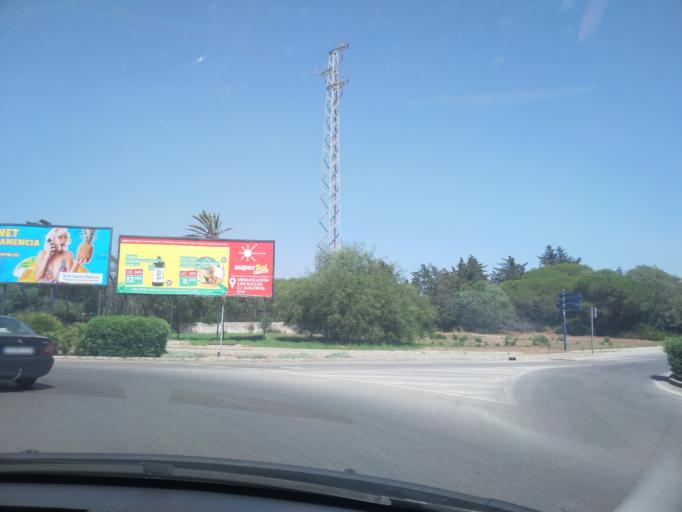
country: ES
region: Andalusia
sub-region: Provincia de Cadiz
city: Chiclana de la Frontera
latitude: 36.3835
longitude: -6.1896
